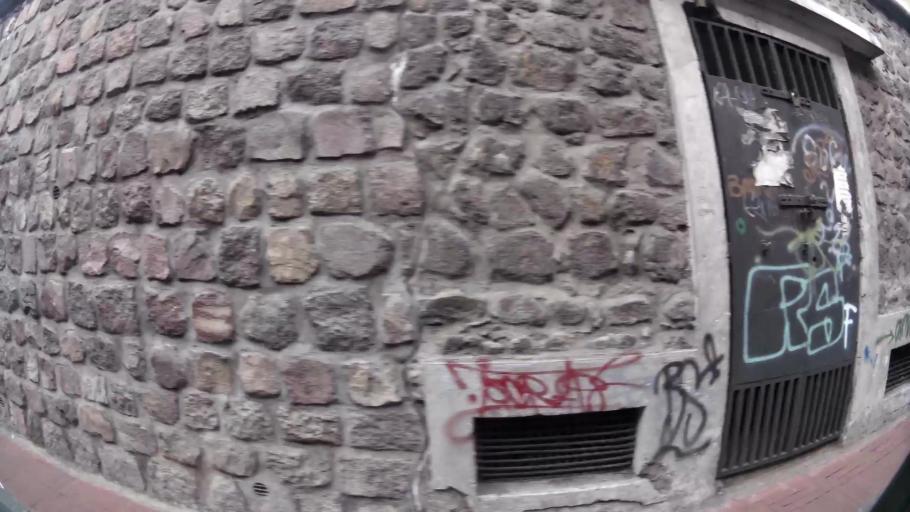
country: EC
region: Pichincha
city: Quito
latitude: -0.2242
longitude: -78.5171
